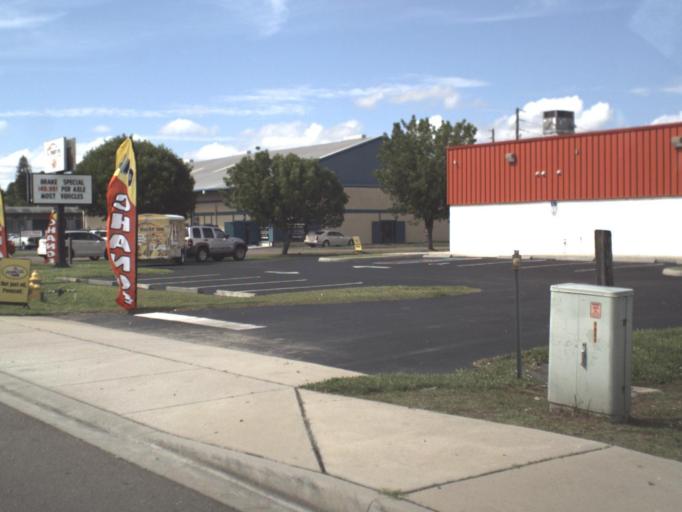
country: US
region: Florida
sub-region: Lee County
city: Fort Myers
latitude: 26.6227
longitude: -81.8615
